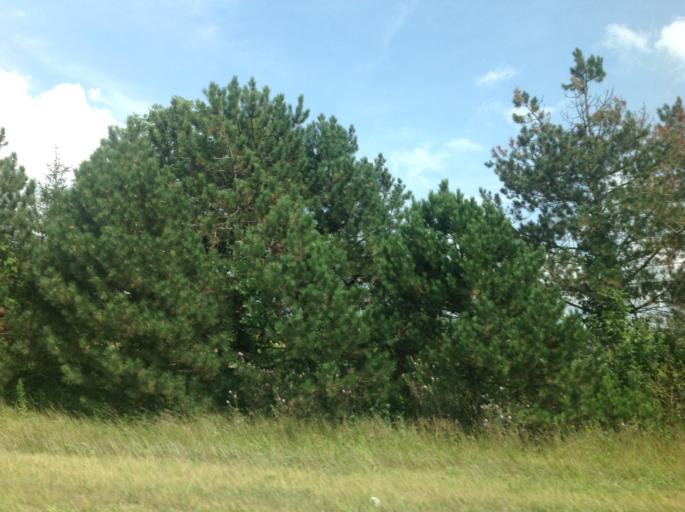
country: US
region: Ohio
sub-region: Morrow County
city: Cardington
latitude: 40.4016
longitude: -82.8223
